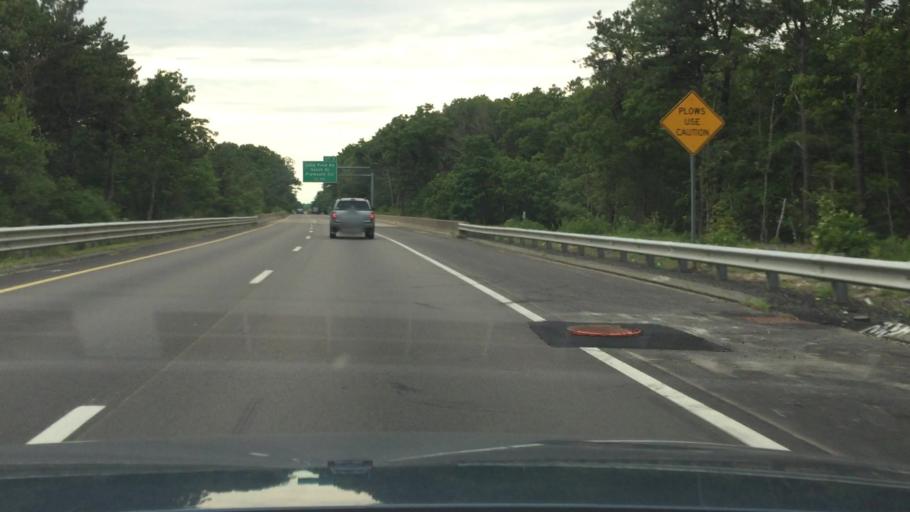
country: US
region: Massachusetts
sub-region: Plymouth County
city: Plymouth
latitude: 41.9320
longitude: -70.6409
